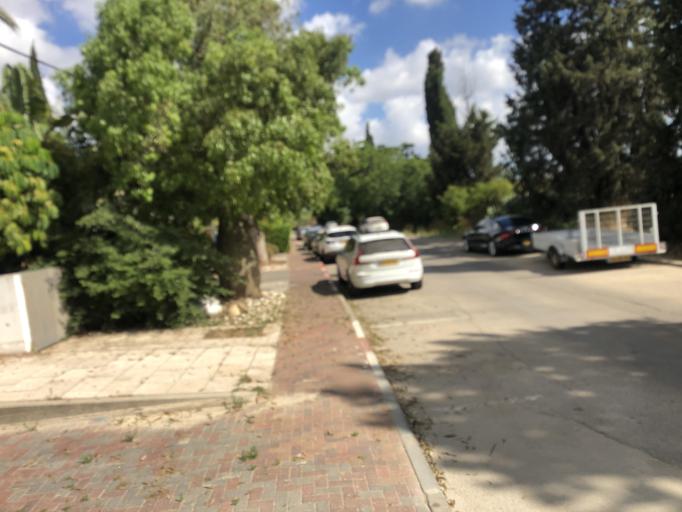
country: IL
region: Central District
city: Yehud
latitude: 32.0385
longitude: 34.8984
